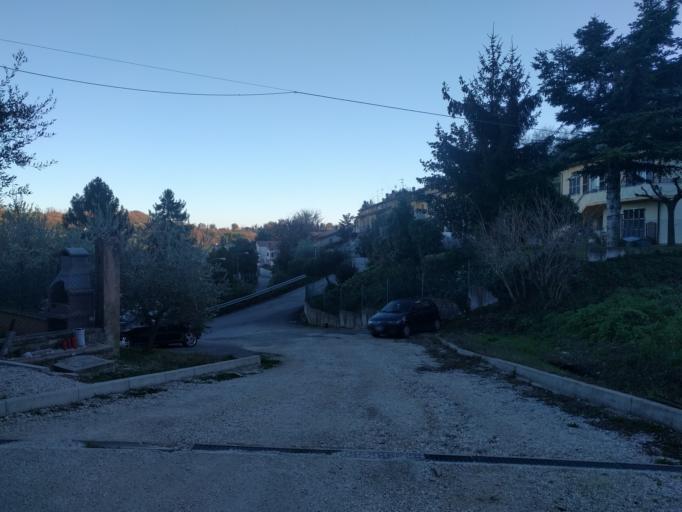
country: IT
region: The Marches
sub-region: Provincia di Pesaro e Urbino
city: Cartoceto
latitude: 43.7659
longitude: 12.8806
